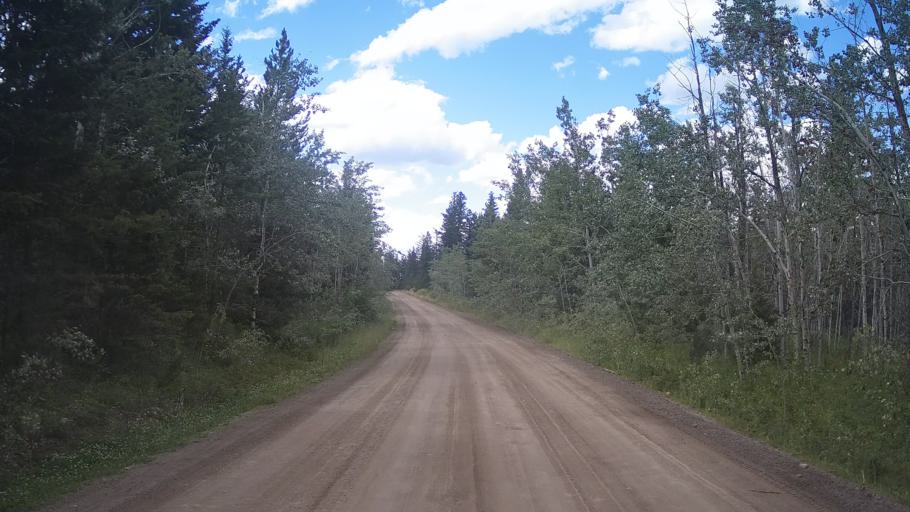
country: CA
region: British Columbia
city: Lillooet
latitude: 51.3333
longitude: -121.8984
